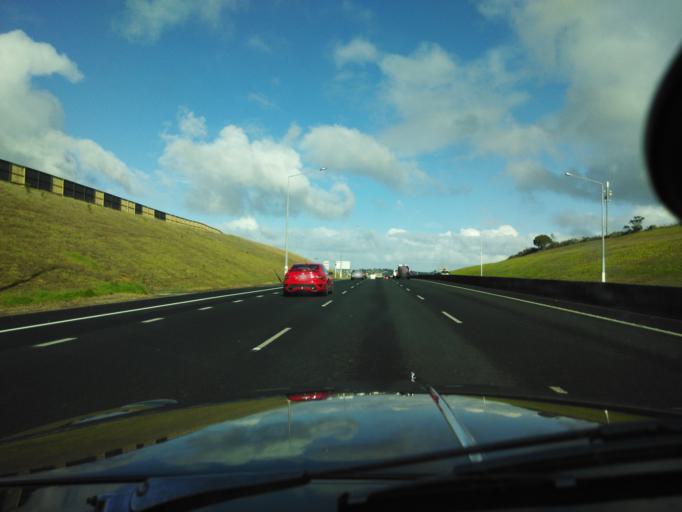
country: NZ
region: Auckland
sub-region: Auckland
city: Rothesay Bay
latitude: -36.7271
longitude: 174.7150
